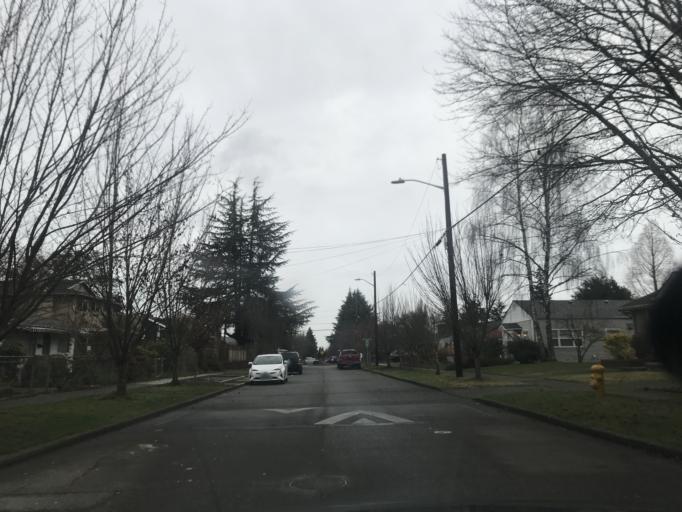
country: US
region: Washington
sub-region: King County
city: White Center
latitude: 47.5238
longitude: -122.3564
